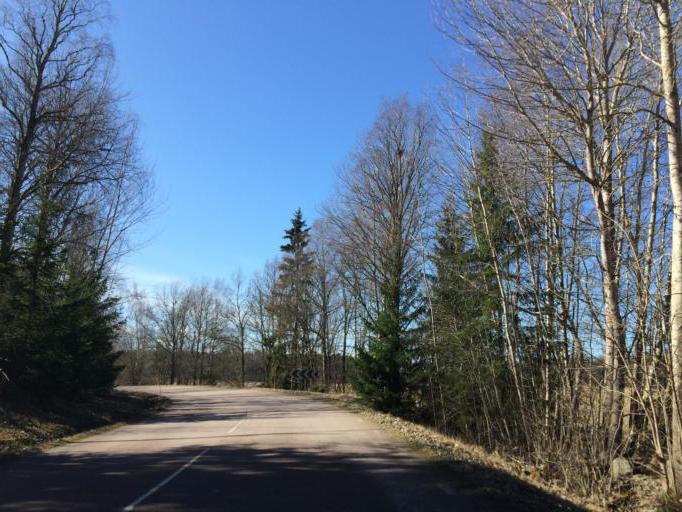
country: SE
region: Vaestmanland
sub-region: Hallstahammars Kommun
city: Kolback
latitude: 59.5056
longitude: 16.2804
